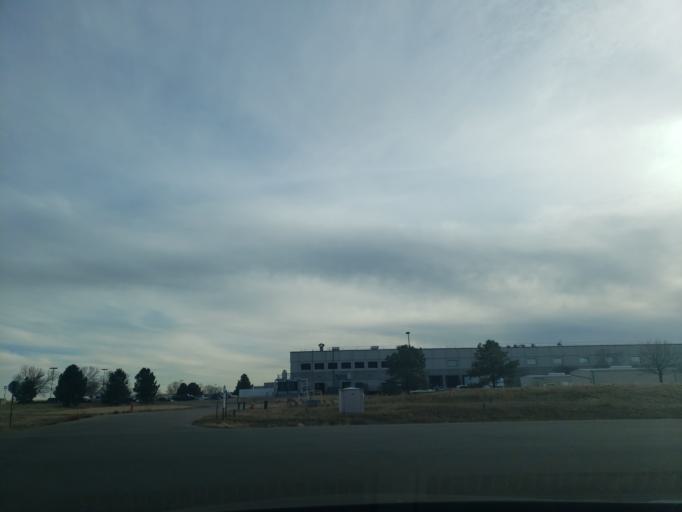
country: US
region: Colorado
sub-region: Larimer County
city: Loveland
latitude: 40.4504
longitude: -104.9991
